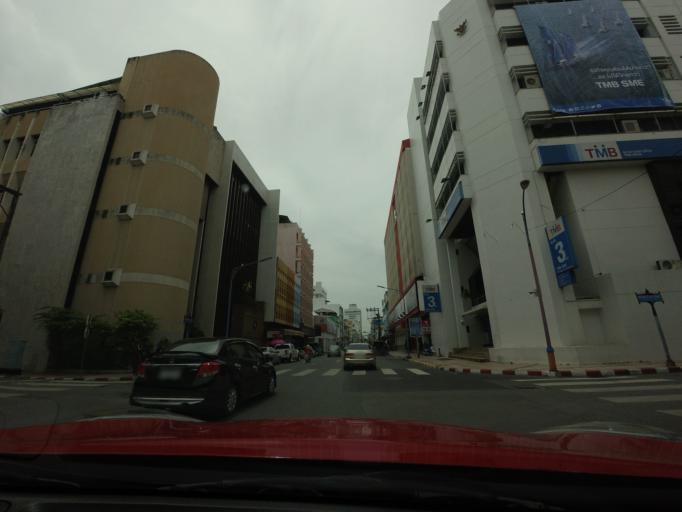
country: TH
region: Songkhla
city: Hat Yai
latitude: 7.0018
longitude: 100.4705
